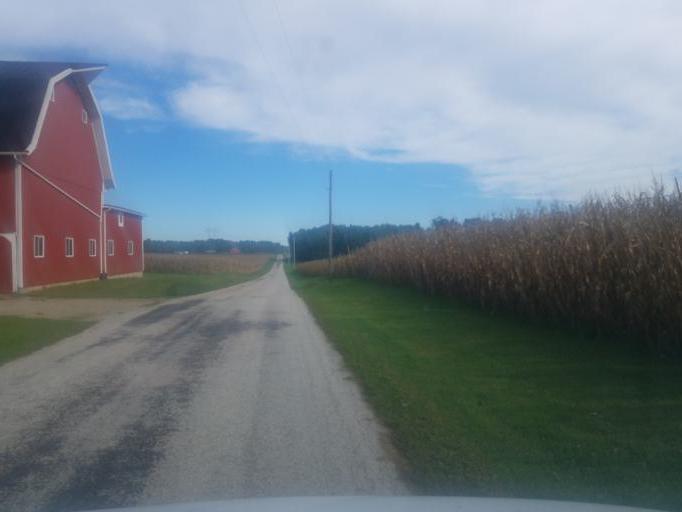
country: US
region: Ohio
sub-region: Crawford County
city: Galion
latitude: 40.6278
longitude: -82.7090
